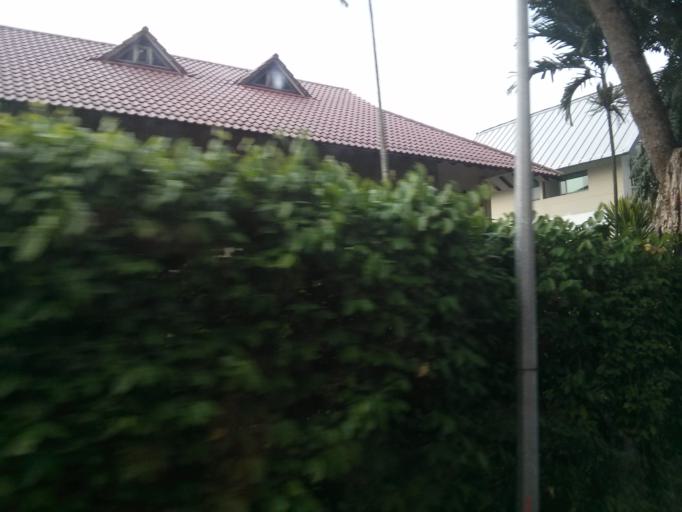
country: SG
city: Singapore
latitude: 1.3426
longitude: 103.8371
